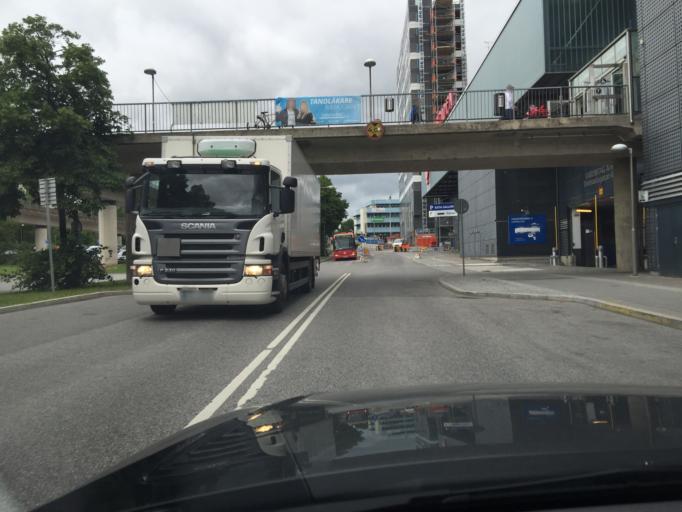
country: SE
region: Stockholm
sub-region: Stockholms Kommun
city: Kista
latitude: 59.4037
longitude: 17.9426
